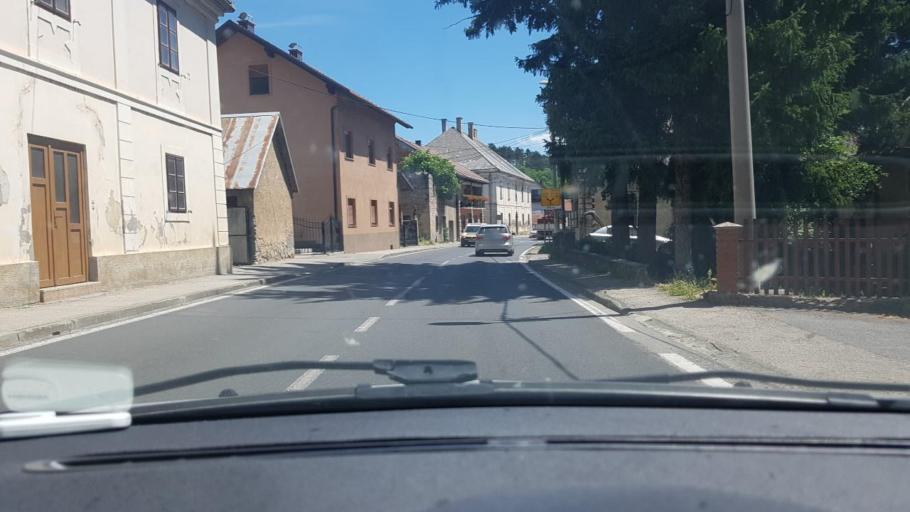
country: HR
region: Licko-Senjska
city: Otocac
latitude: 44.8718
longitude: 15.2272
